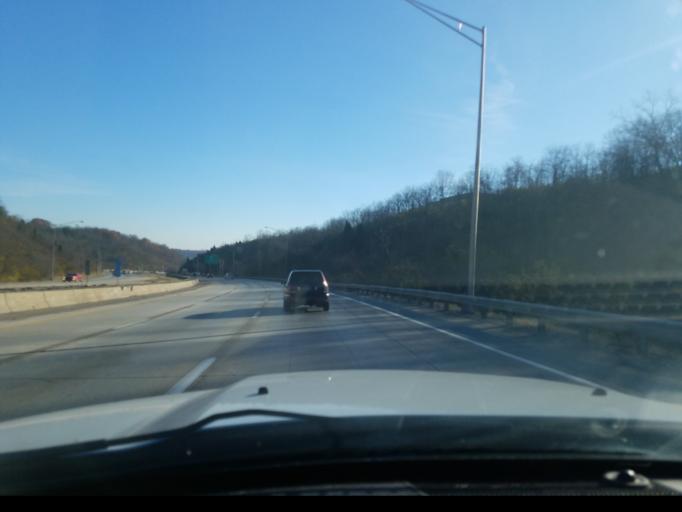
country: US
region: Kentucky
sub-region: Kenton County
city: Lakeside Park
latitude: 39.0252
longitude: -84.5607
